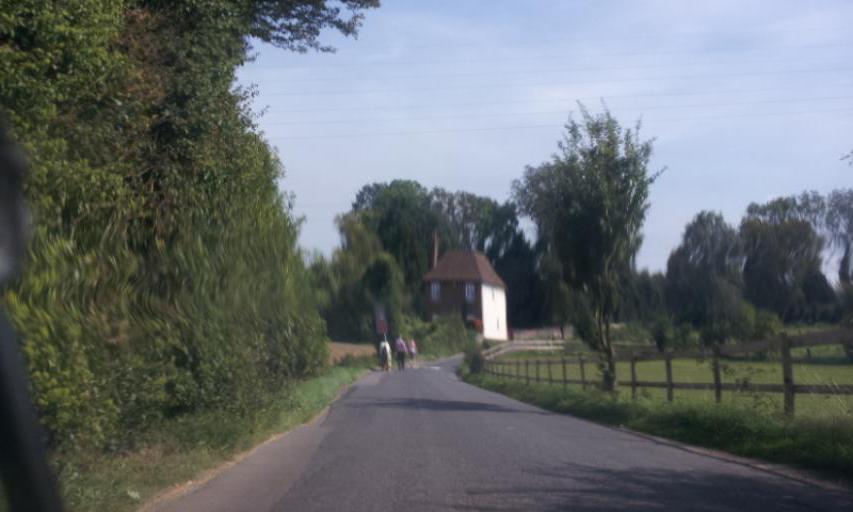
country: GB
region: England
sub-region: Kent
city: Newington
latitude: 51.3423
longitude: 0.6952
